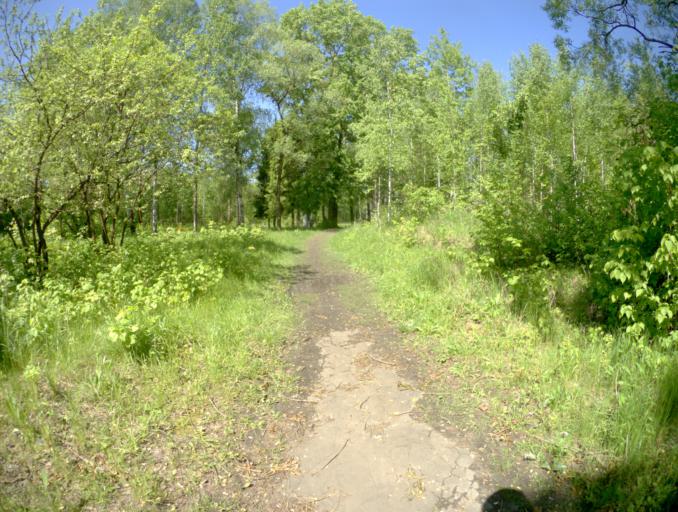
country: RU
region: Vladimir
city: Gusevskiy
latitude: 55.7209
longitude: 40.5644
